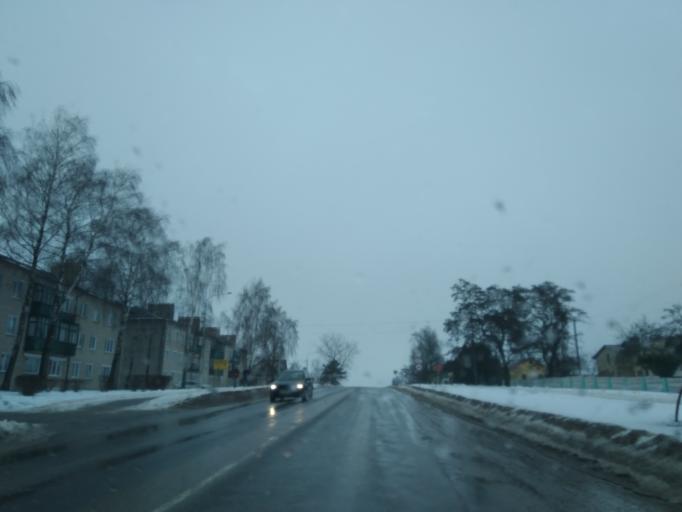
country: BY
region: Minsk
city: Nyasvizh
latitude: 53.2315
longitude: 26.6556
